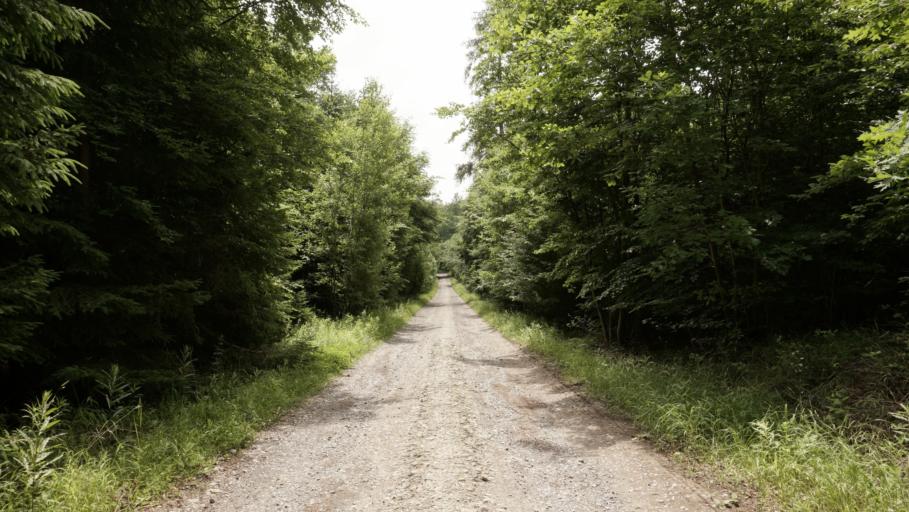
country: DE
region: Baden-Wuerttemberg
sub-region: Karlsruhe Region
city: Mosbach
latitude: 49.3290
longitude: 9.1919
